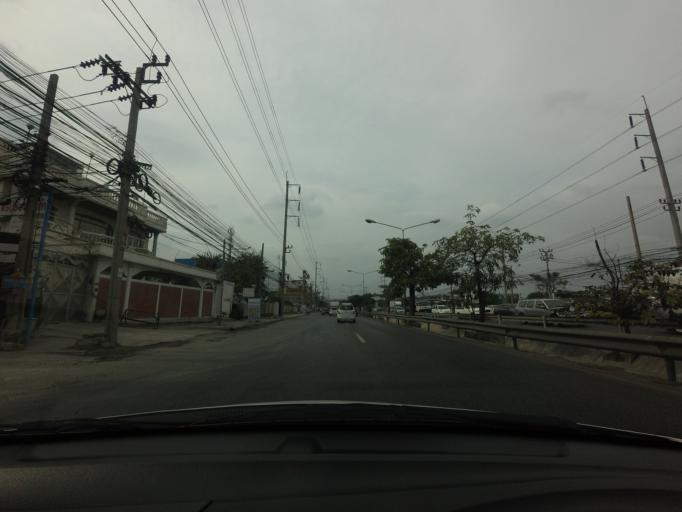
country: TH
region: Samut Prakan
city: Samut Prakan
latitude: 13.5337
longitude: 100.6286
